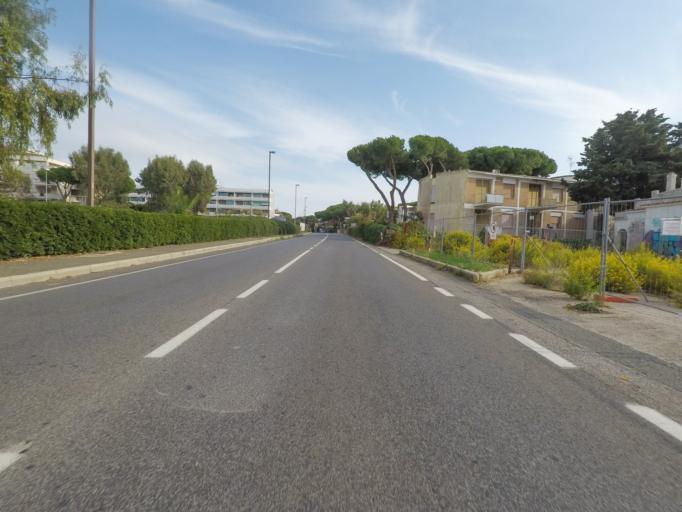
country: IT
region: Latium
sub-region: Citta metropolitana di Roma Capitale
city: Santa Marinella
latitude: 42.0340
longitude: 11.8357
